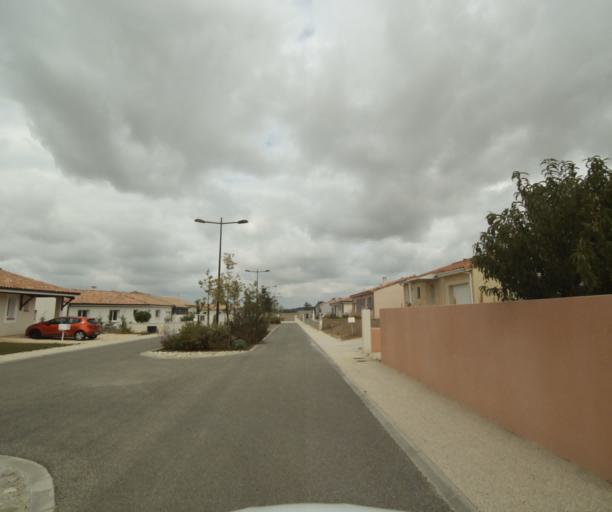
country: FR
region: Midi-Pyrenees
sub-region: Departement de la Haute-Garonne
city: Villefranche-de-Lauragais
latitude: 43.4123
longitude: 1.7133
